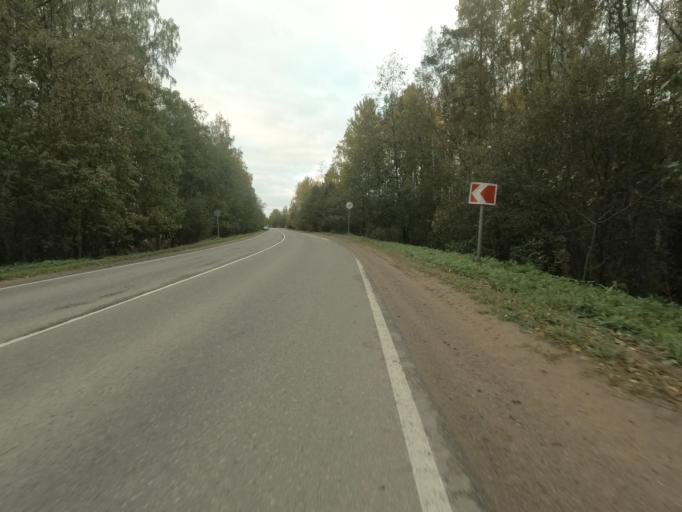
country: RU
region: Leningrad
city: Pavlovo
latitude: 59.8013
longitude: 30.9412
